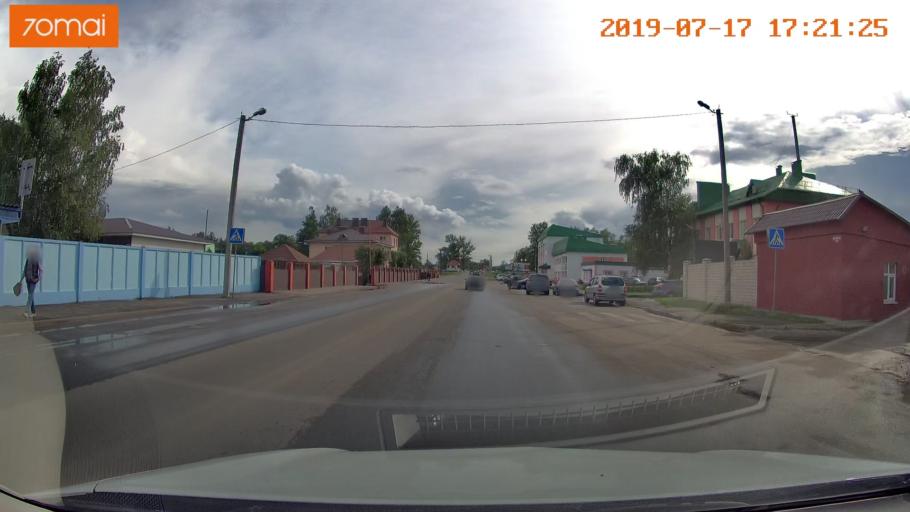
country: BY
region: Mogilev
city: Babruysk
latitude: 53.1479
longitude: 29.1788
